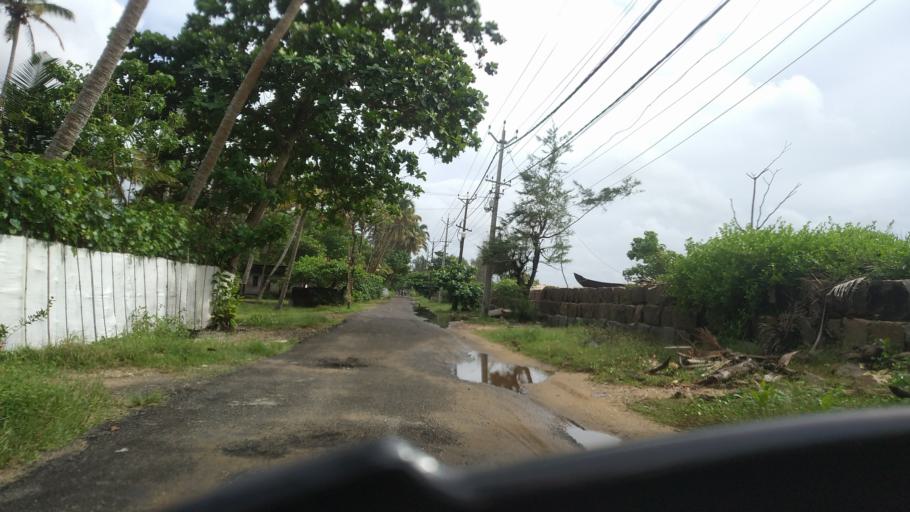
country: IN
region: Kerala
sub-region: Thrissur District
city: Kodungallur
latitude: 10.1309
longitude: 76.1819
